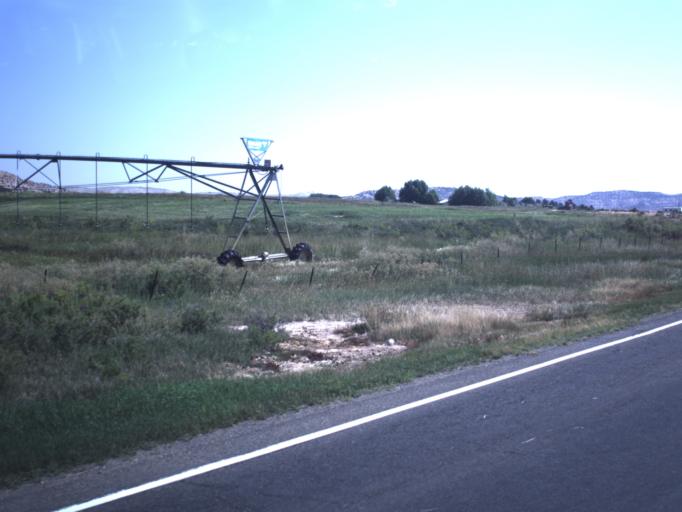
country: US
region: Utah
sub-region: Daggett County
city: Manila
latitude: 40.9889
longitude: -109.6932
